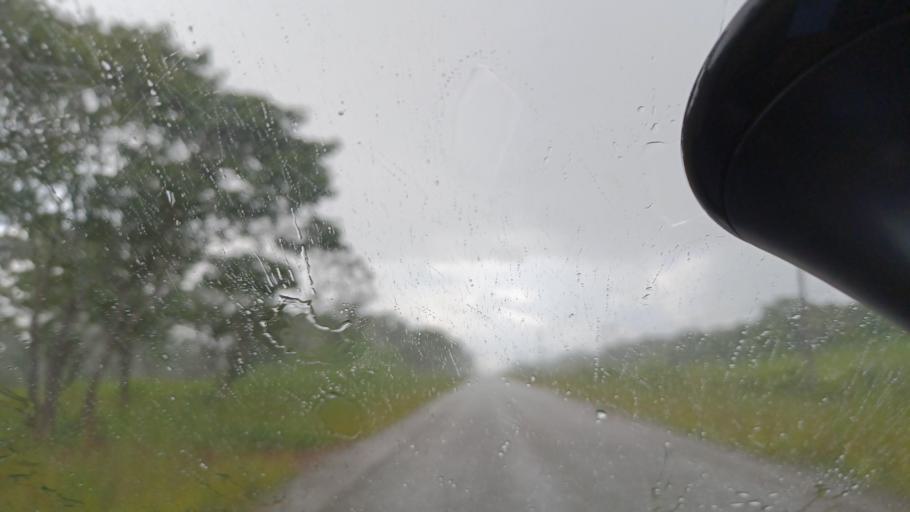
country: ZM
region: North-Western
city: Kasempa
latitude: -13.0933
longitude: 25.9207
